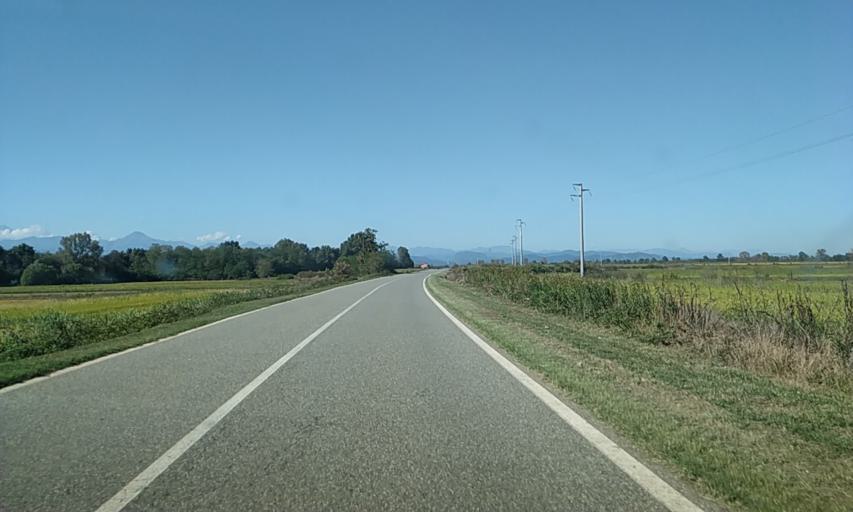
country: IT
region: Piedmont
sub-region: Provincia di Vercelli
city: San Giacomo Vercellese
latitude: 45.5040
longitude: 8.3242
